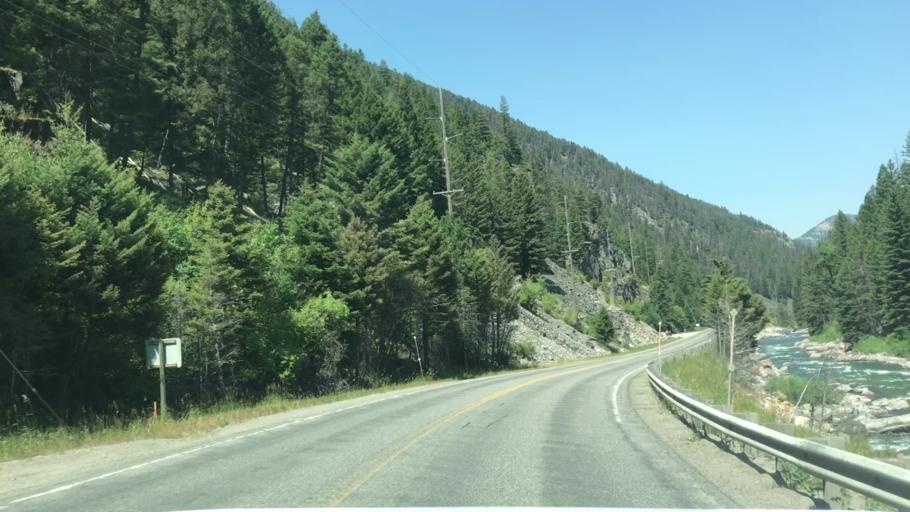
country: US
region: Montana
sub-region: Gallatin County
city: Big Sky
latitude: 45.4159
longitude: -111.2326
